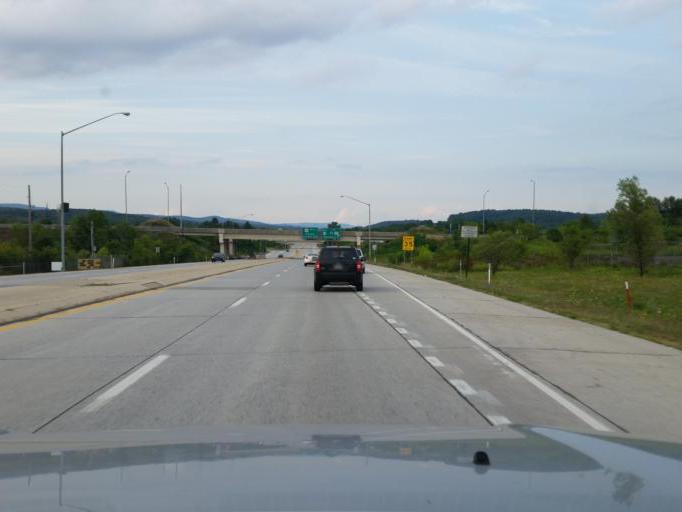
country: US
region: Pennsylvania
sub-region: Blair County
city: Duncansville
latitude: 40.4390
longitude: -78.4351
